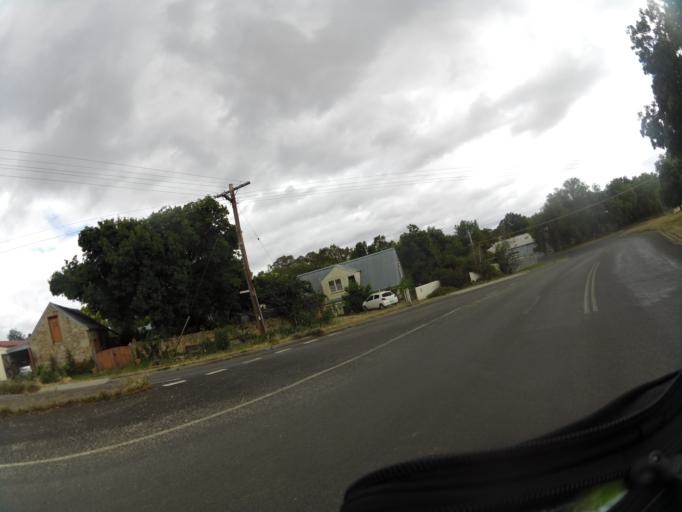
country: AU
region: Victoria
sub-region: Mount Alexander
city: Castlemaine
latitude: -37.0722
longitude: 144.2104
